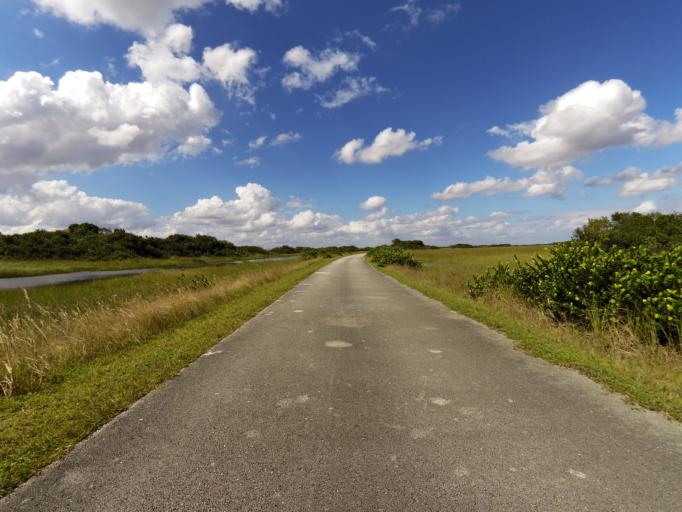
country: US
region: Florida
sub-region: Miami-Dade County
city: The Hammocks
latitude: 25.6970
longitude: -80.7623
